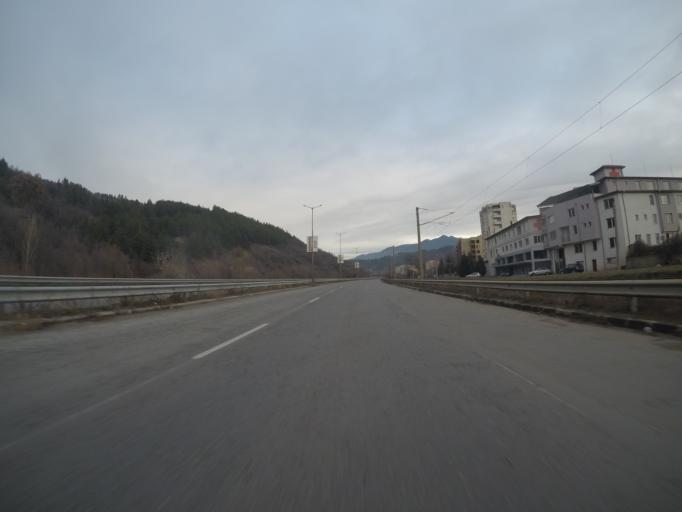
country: BG
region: Kyustendil
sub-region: Obshtina Dupnitsa
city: Dupnitsa
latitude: 42.2682
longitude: 23.1140
